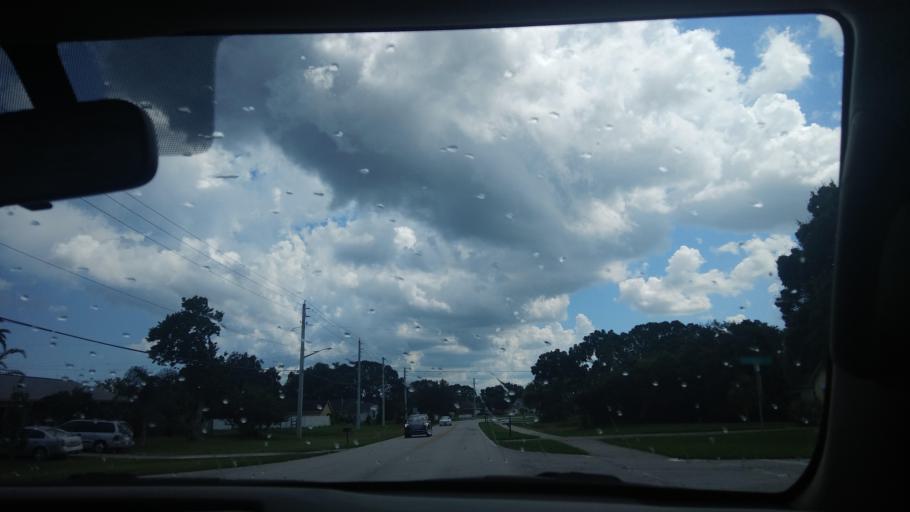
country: US
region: Florida
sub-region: Brevard County
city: Palm Bay
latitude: 28.0068
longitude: -80.6455
